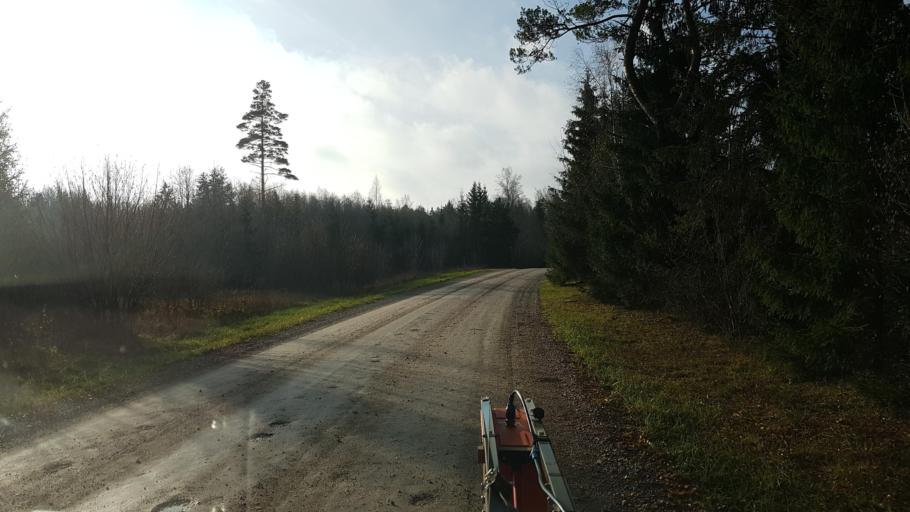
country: EE
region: Harju
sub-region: Nissi vald
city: Turba
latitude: 59.1842
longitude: 24.1411
